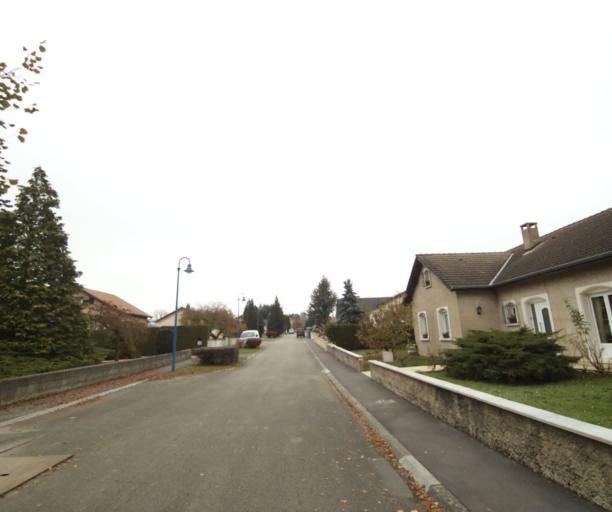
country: FR
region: Lorraine
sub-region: Departement de Meurthe-et-Moselle
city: Mancieulles
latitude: 49.2694
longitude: 5.9150
